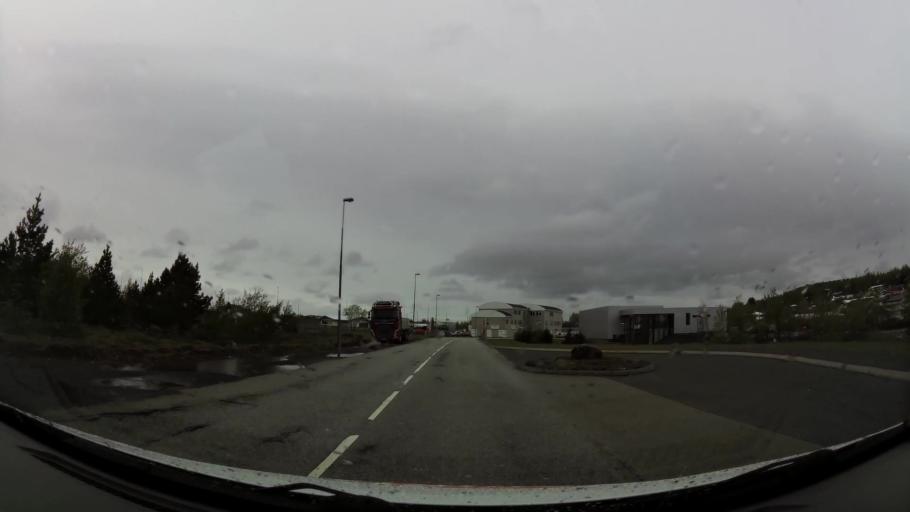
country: IS
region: Capital Region
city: Hafnarfjoerdur
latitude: 64.0654
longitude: -21.9345
